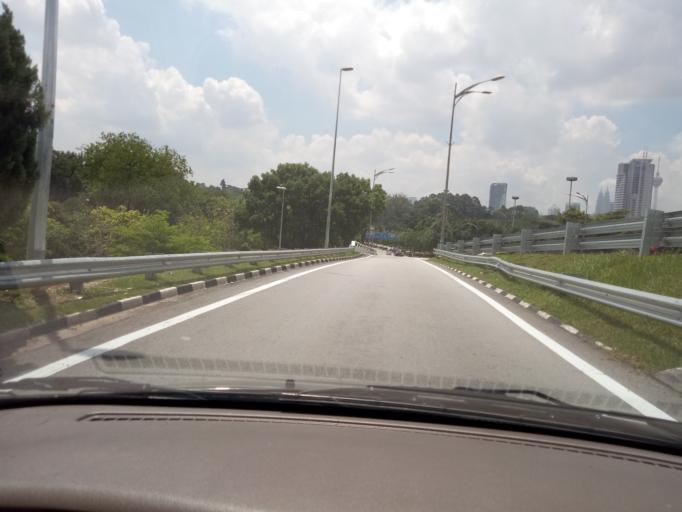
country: MY
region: Kuala Lumpur
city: Kuala Lumpur
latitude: 3.1458
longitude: 101.6780
